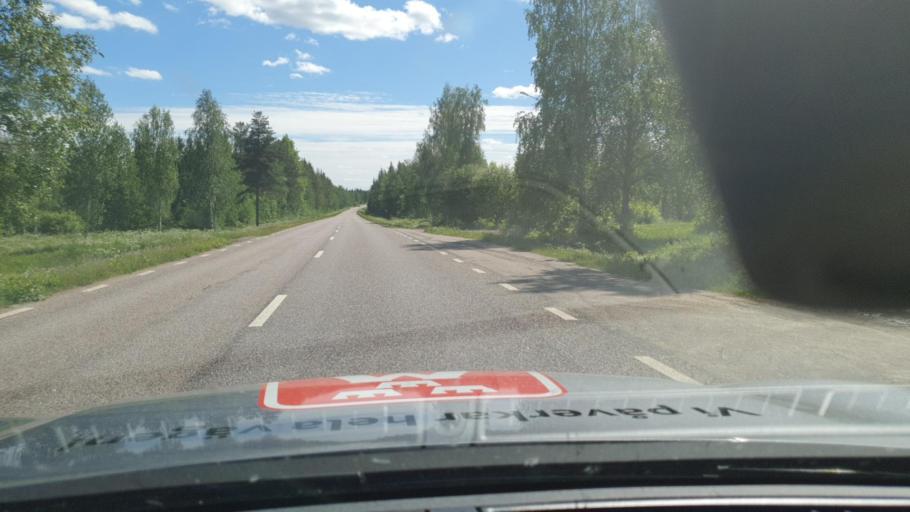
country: FI
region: Lapland
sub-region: Tunturi-Lappi
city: Kolari
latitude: 67.0676
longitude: 23.6649
